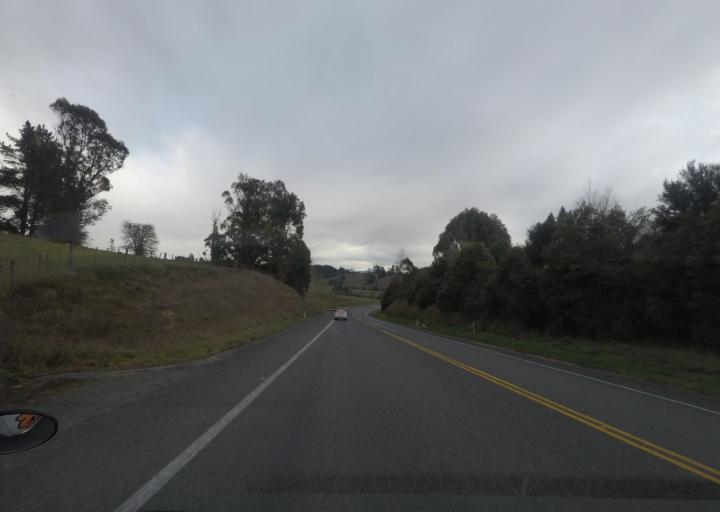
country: NZ
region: Tasman
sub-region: Tasman District
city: Mapua
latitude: -41.2824
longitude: 173.0737
